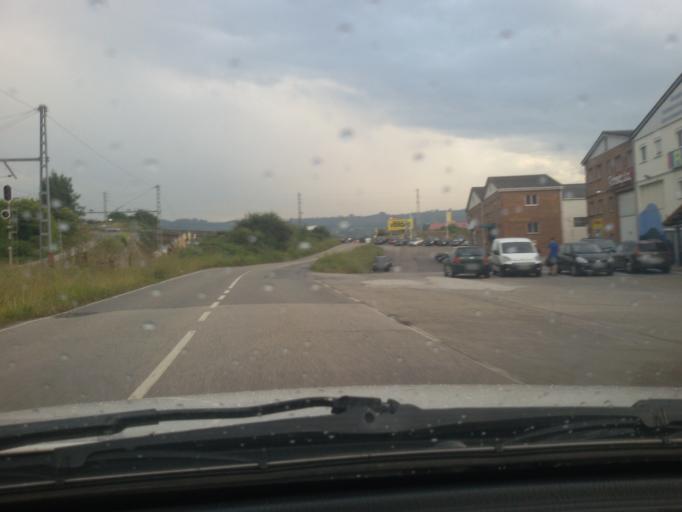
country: ES
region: Asturias
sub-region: Province of Asturias
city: Lugones
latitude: 43.3877
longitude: -5.7852
